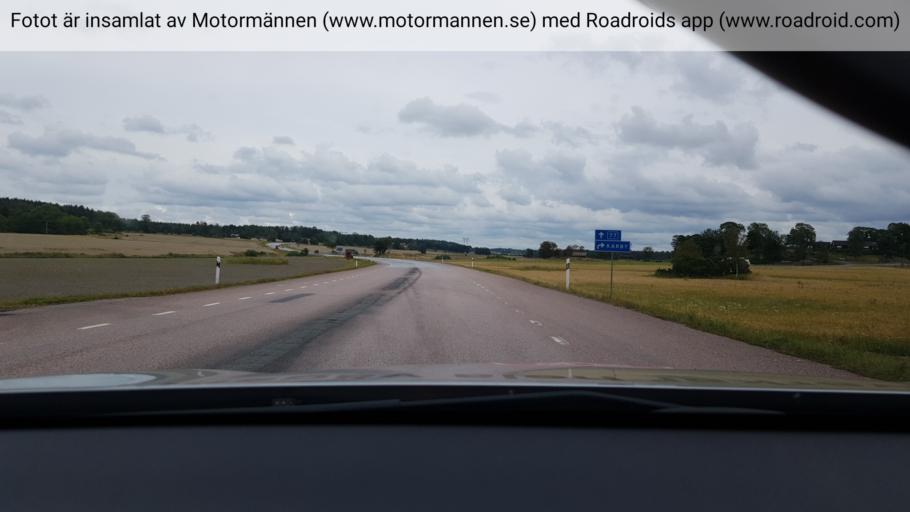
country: SE
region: Stockholm
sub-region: Sigtuna Kommun
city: Marsta
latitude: 59.7487
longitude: 17.9556
